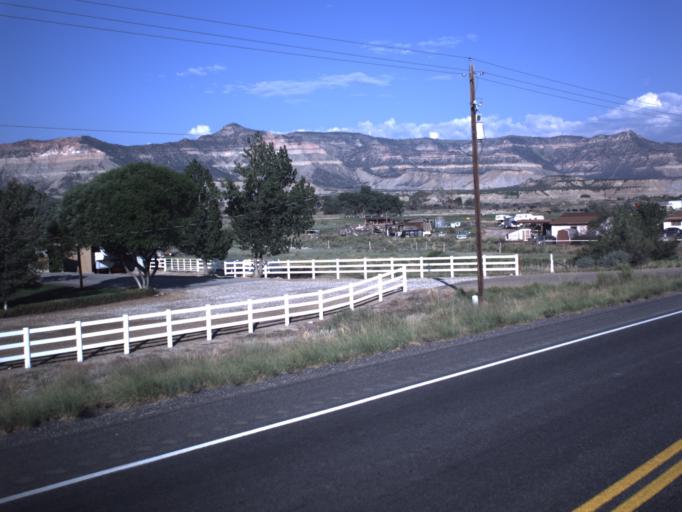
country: US
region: Utah
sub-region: Emery County
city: Huntington
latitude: 39.3427
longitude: -110.9833
